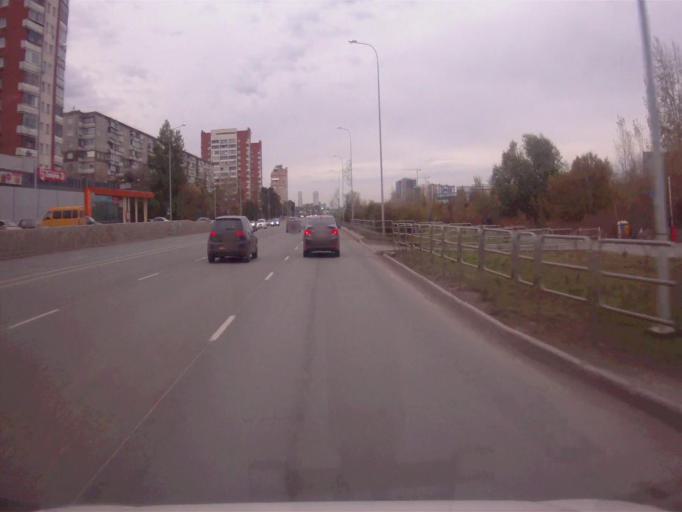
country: RU
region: Chelyabinsk
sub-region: Gorod Chelyabinsk
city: Chelyabinsk
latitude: 55.1743
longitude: 61.3405
